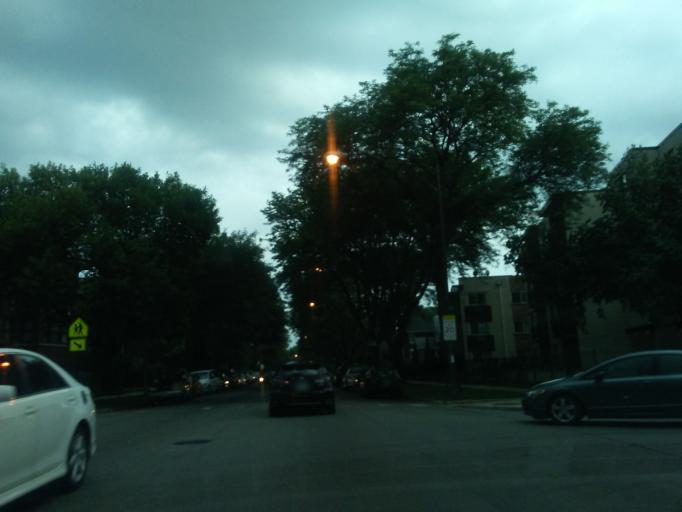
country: US
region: Illinois
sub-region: Cook County
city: Evanston
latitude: 42.0113
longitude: -87.6828
